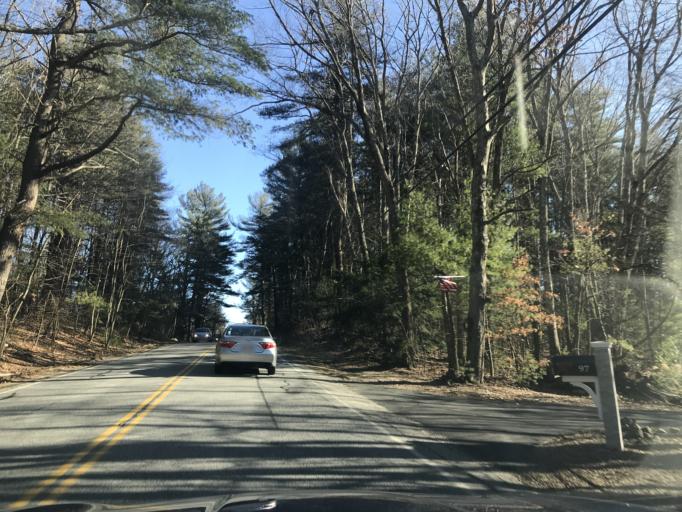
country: US
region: Massachusetts
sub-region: Essex County
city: Groveland
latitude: 42.7118
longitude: -71.0354
